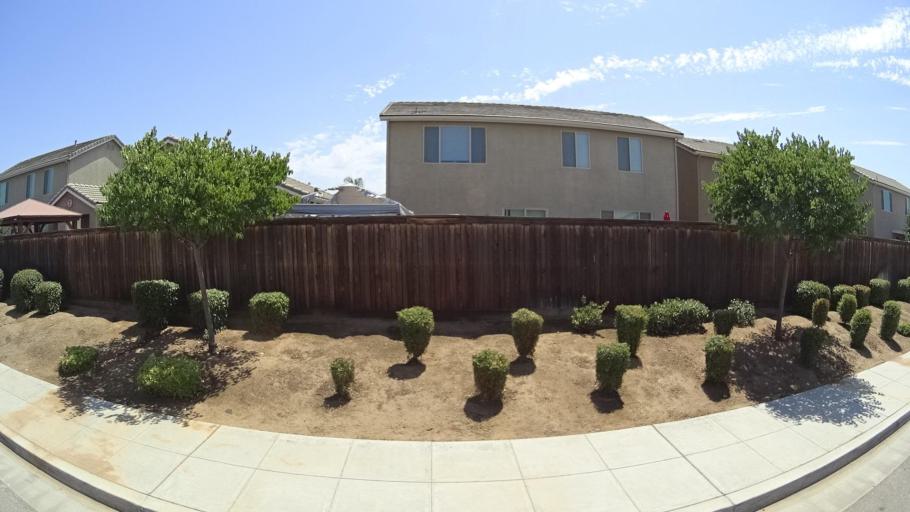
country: US
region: California
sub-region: Fresno County
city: Tarpey Village
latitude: 36.7803
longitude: -119.6595
